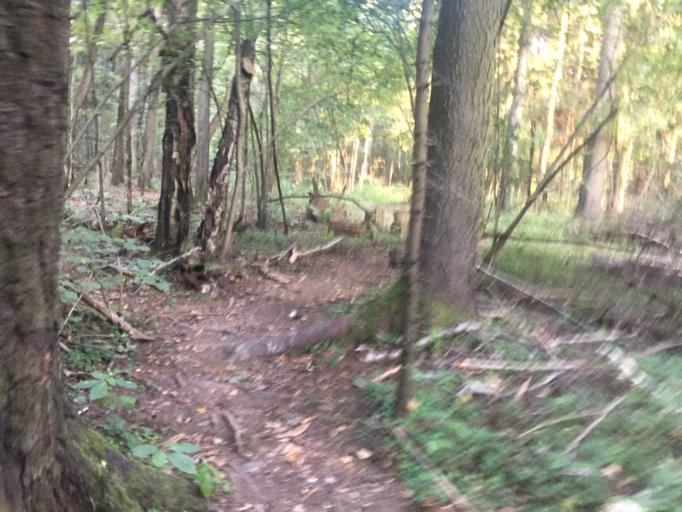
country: RU
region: Moscow
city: Gol'yanovo
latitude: 55.8498
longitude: 37.8122
